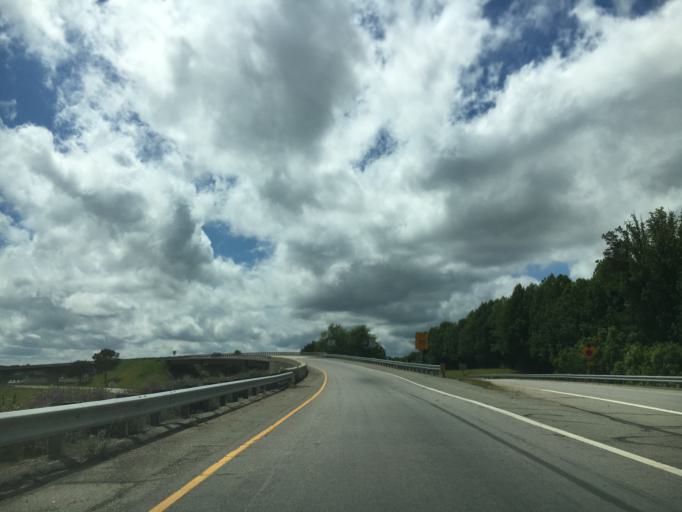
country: US
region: Virginia
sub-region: Mecklenburg County
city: Clarksville
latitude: 36.6351
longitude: -78.5367
